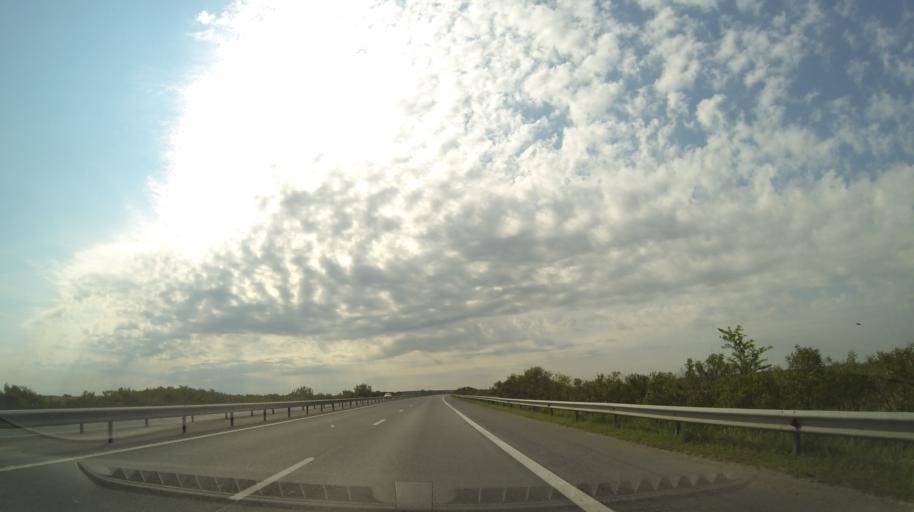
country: RO
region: Arges
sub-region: Comuna Cateasca
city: Cateasca
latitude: 44.7507
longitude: 25.0938
